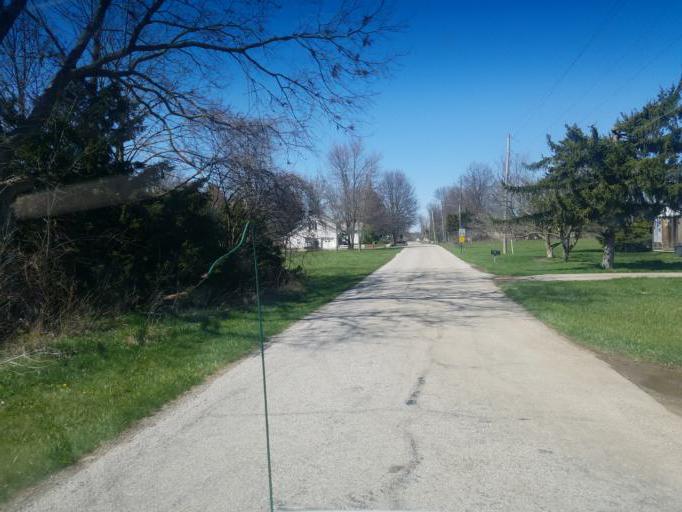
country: US
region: Ohio
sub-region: Morrow County
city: Cardington
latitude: 40.4964
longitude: -82.9018
